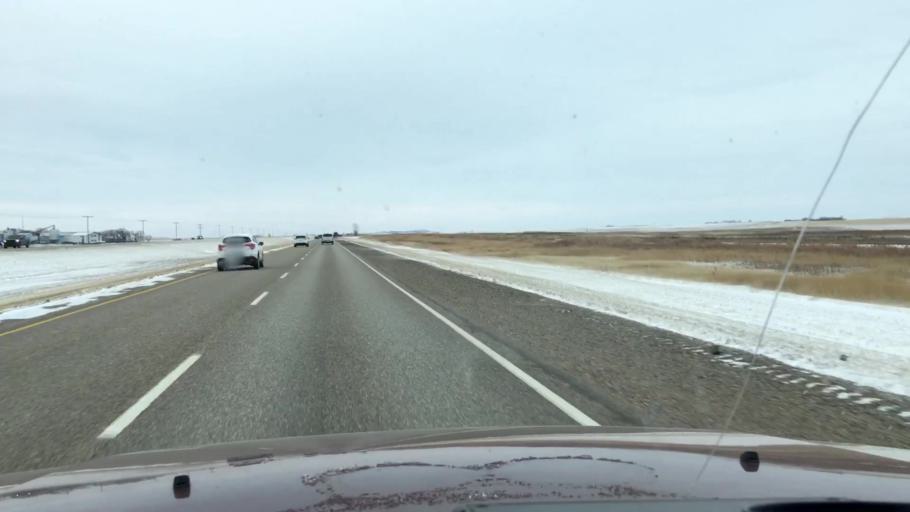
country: CA
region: Saskatchewan
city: Moose Jaw
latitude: 51.0129
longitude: -105.7781
